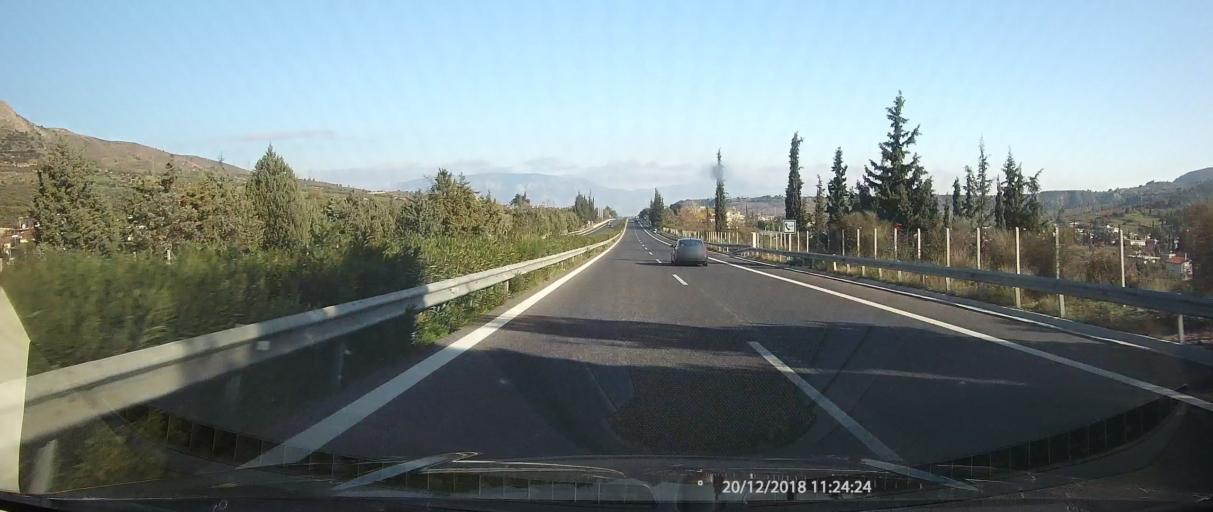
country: GR
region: Peloponnese
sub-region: Nomos Korinthias
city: Arkhaia Korinthos
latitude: 37.8774
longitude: 22.8823
